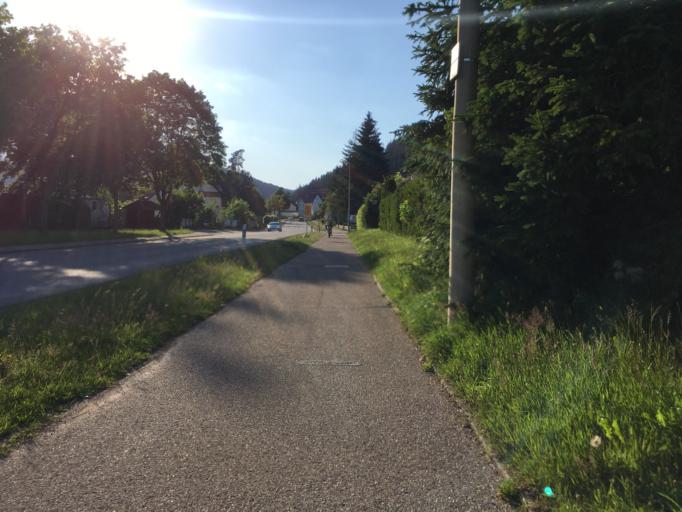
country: DE
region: Baden-Wuerttemberg
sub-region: Freiburg Region
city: Titisee-Neustadt
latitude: 47.9217
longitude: 8.2013
